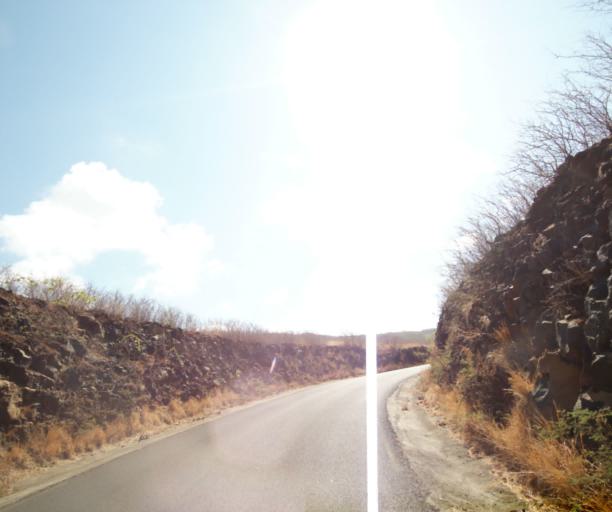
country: RE
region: Reunion
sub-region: Reunion
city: Trois-Bassins
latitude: -21.1020
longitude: 55.2505
